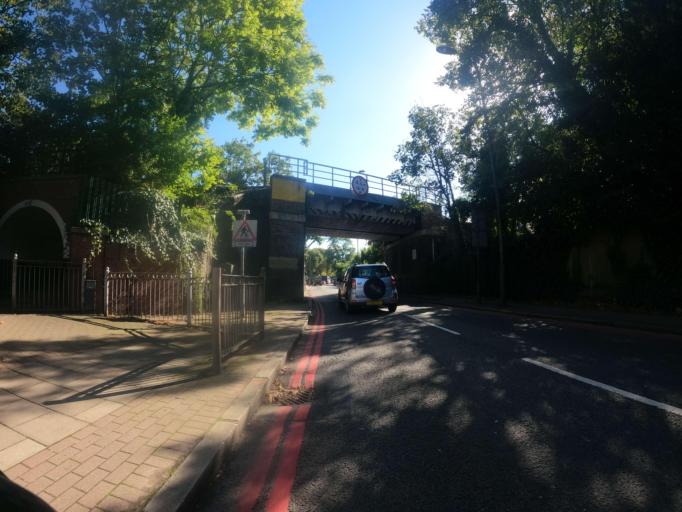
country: GB
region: England
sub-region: Greater London
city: Brentford
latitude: 51.4806
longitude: -0.2832
